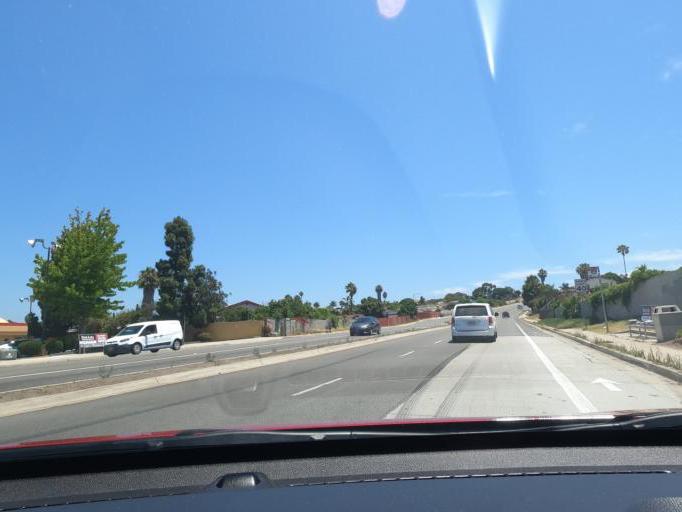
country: US
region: California
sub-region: San Diego County
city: Imperial Beach
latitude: 32.5733
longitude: -117.0538
